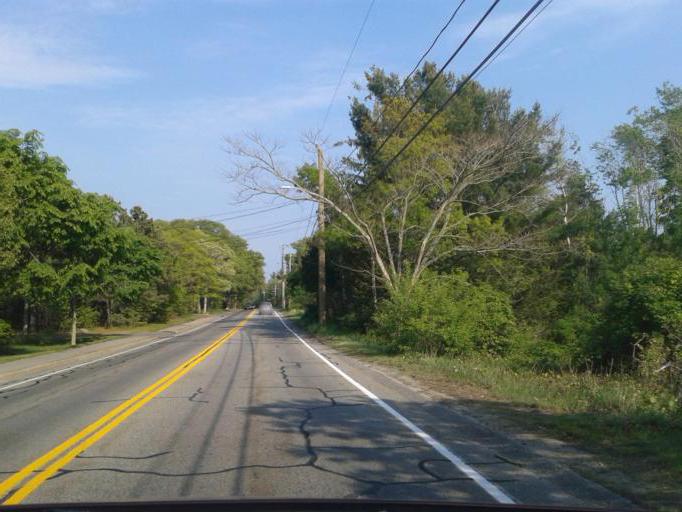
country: US
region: Massachusetts
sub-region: Barnstable County
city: Teaticket
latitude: 41.5848
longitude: -70.6036
